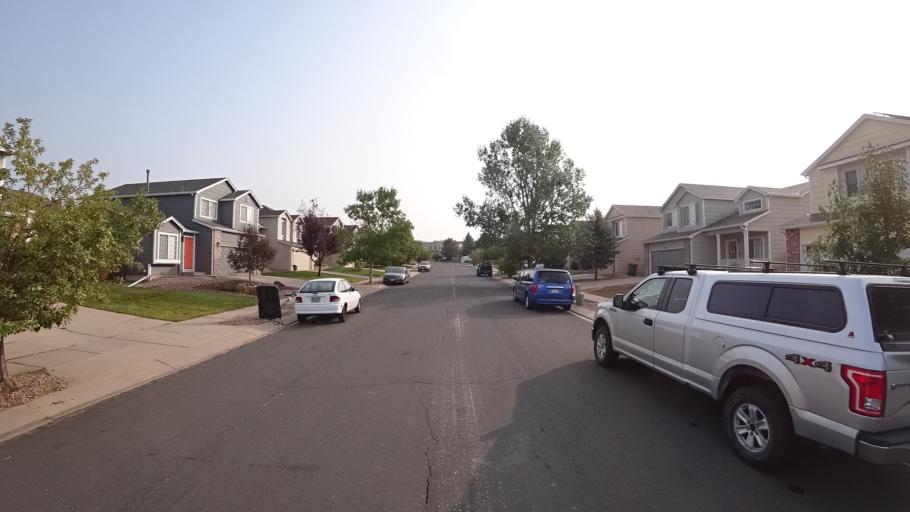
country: US
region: Colorado
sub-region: El Paso County
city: Cimarron Hills
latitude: 38.9337
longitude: -104.7266
